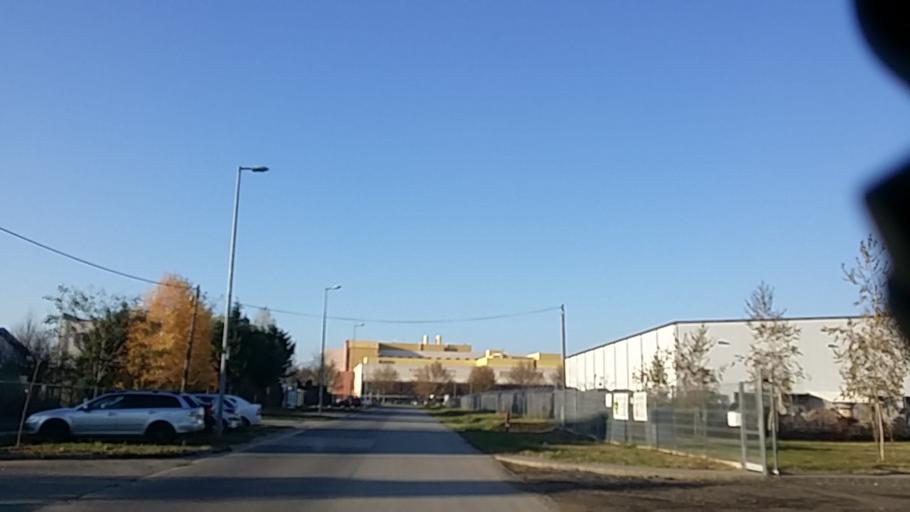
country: HU
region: Budapest
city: Budapest XVII. keruelet
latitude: 47.4944
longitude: 19.2330
